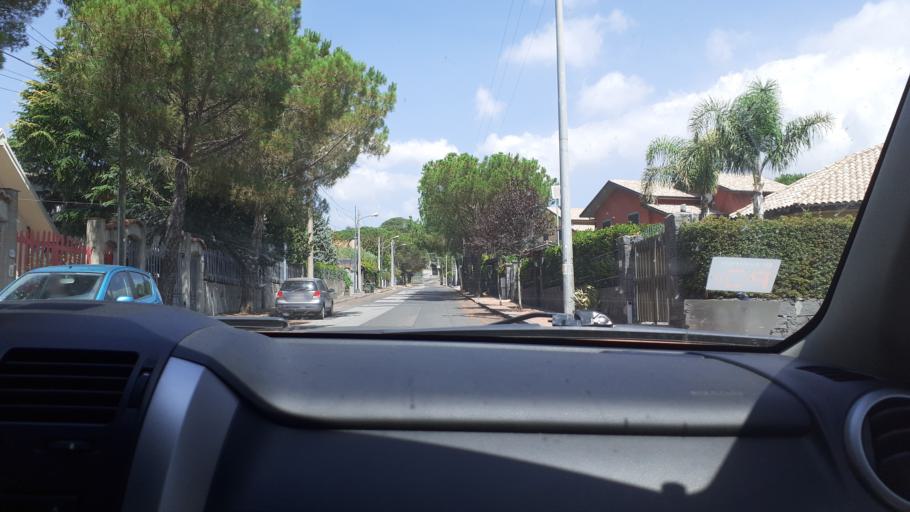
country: IT
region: Sicily
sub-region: Catania
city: Nicolosi
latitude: 37.6225
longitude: 15.0265
